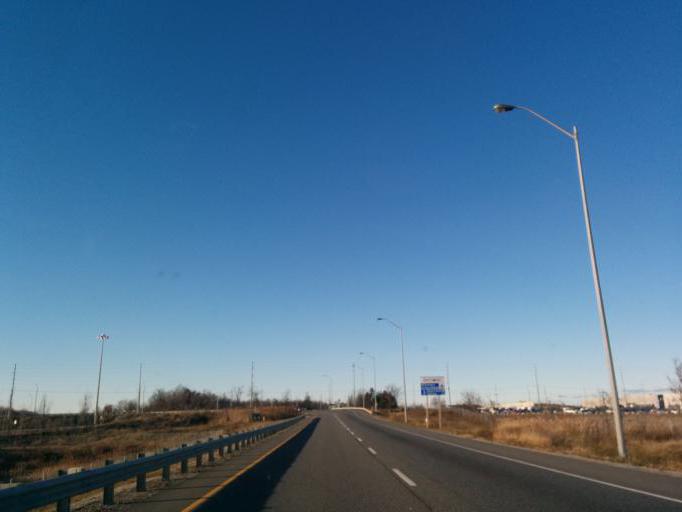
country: CA
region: Ontario
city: Brampton
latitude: 43.7562
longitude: -79.7950
